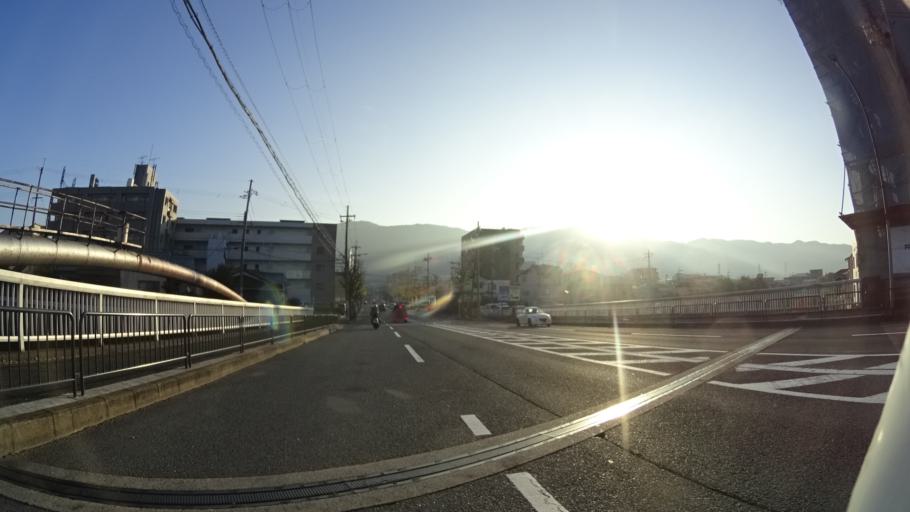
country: JP
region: Shiga Prefecture
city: Otsu-shi
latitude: 34.9718
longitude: 135.8094
